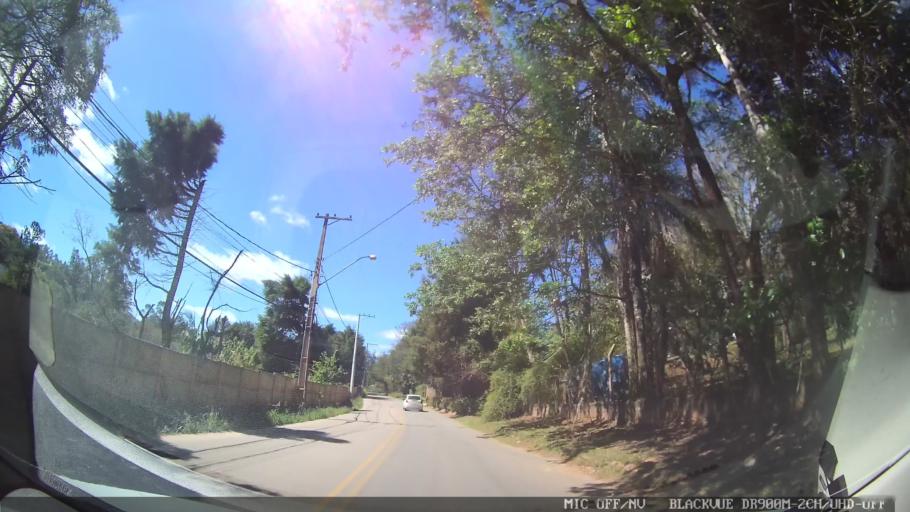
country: BR
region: Sao Paulo
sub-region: Campo Limpo Paulista
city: Campo Limpo Paulista
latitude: -23.1808
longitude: -46.7520
